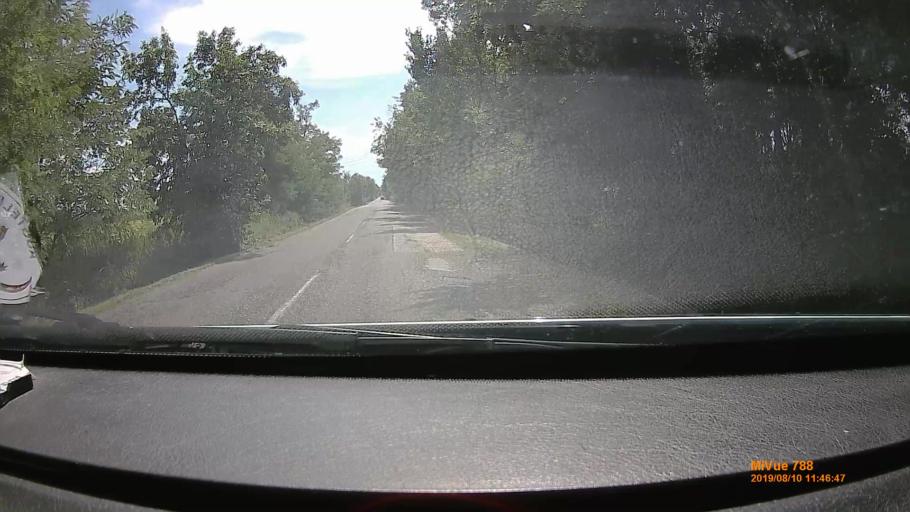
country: HU
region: Borsod-Abauj-Zemplen
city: Szentistvan
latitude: 47.7092
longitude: 20.6312
